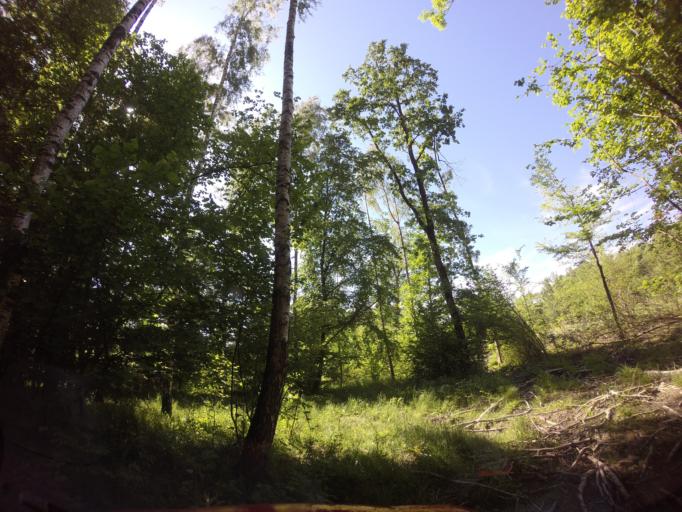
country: PL
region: West Pomeranian Voivodeship
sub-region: Powiat choszczenski
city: Choszczno
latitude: 53.1704
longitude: 15.3531
